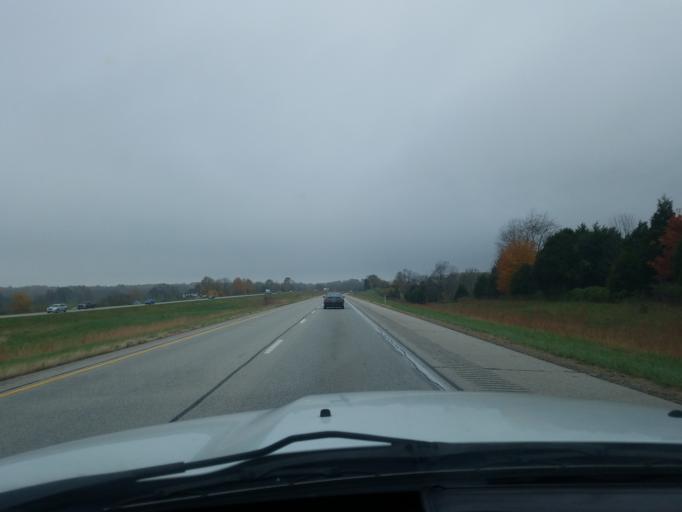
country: US
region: Indiana
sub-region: Harrison County
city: Corydon
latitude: 38.2486
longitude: -86.0645
